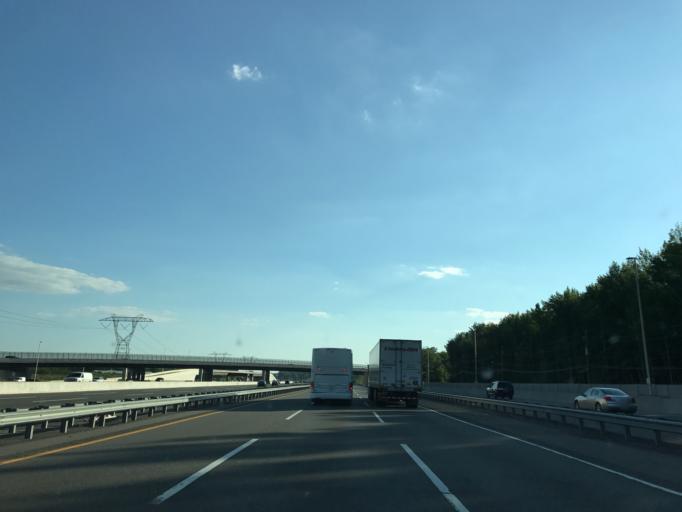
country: US
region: New Jersey
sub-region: Mercer County
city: Yardville
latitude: 40.1733
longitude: -74.6369
